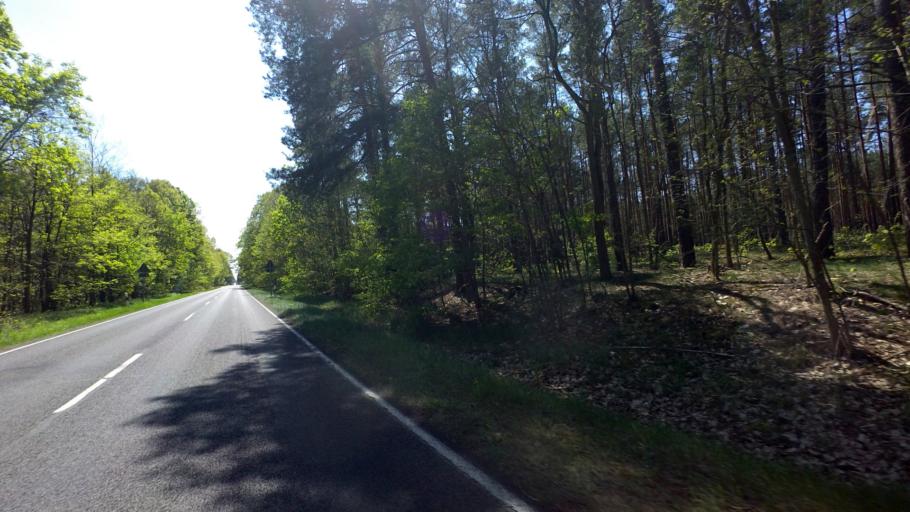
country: DE
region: Brandenburg
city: Bestensee
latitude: 52.2144
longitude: 13.6877
